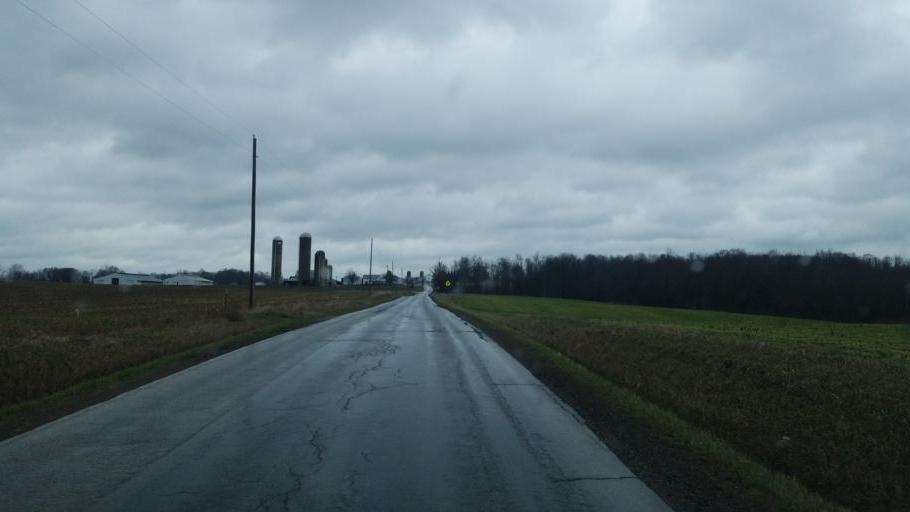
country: US
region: Ohio
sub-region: Wayne County
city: Apple Creek
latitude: 40.6791
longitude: -81.8178
